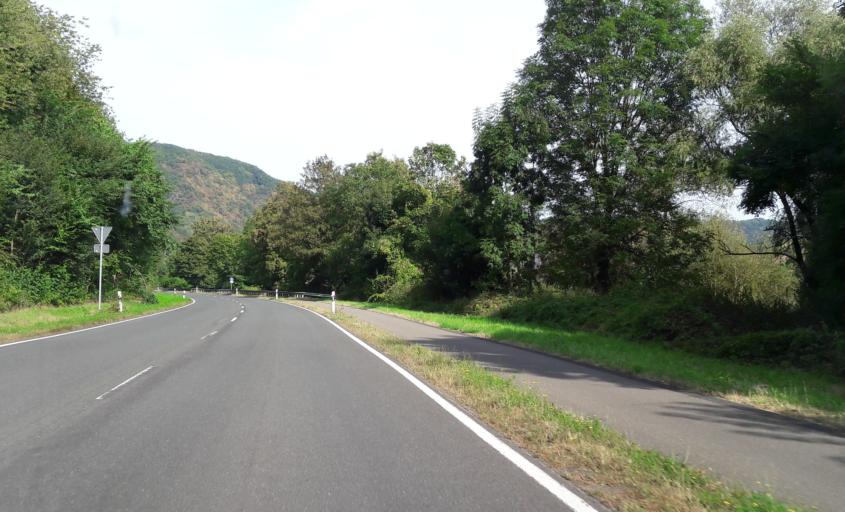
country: DE
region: Rheinland-Pfalz
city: Nehren
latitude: 50.0915
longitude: 7.1969
